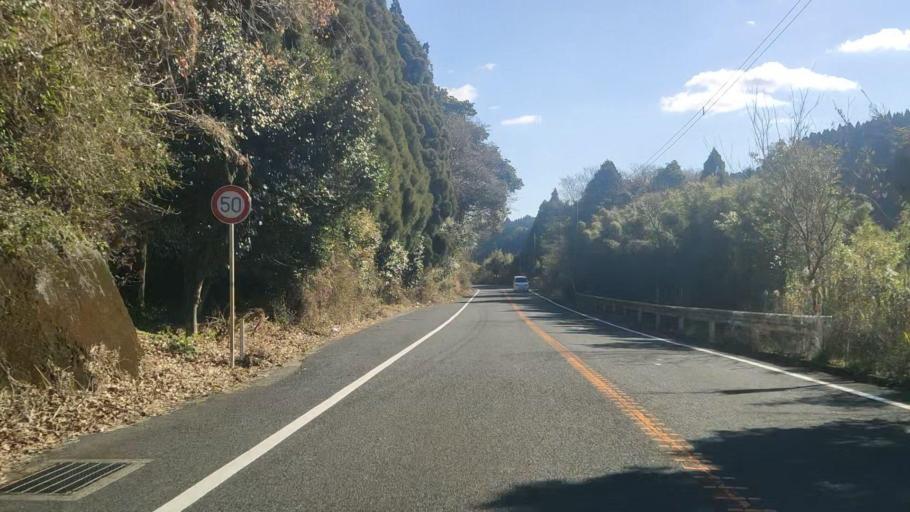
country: JP
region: Kagoshima
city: Sueyoshicho-ninokata
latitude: 31.6622
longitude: 130.8884
